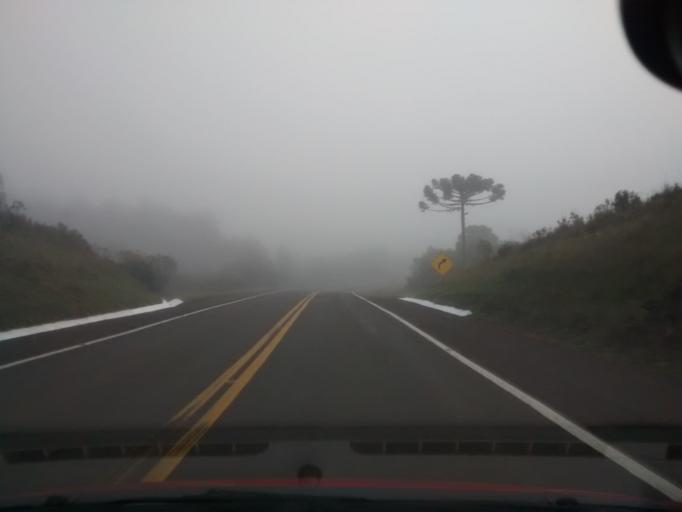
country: BR
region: Rio Grande do Sul
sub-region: Vacaria
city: Vacaria
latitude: -28.2892
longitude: -50.8027
